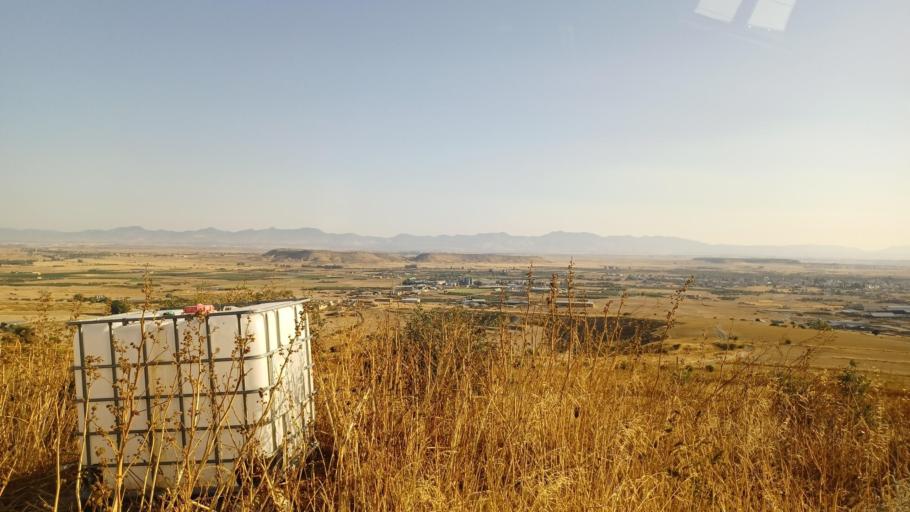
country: CY
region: Larnaka
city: Athienou
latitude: 35.0369
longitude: 33.5230
